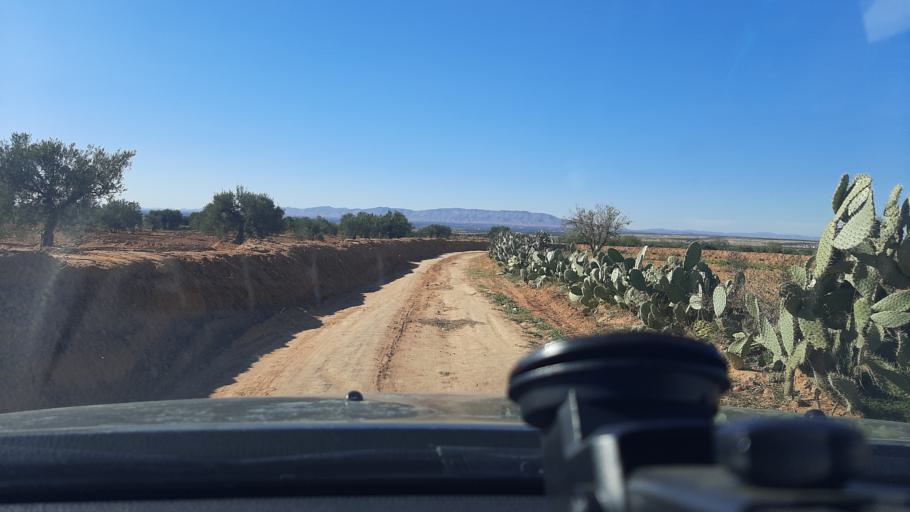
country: TN
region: Safaqis
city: Bi'r `Ali Bin Khalifah
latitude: 34.9994
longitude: 10.0887
